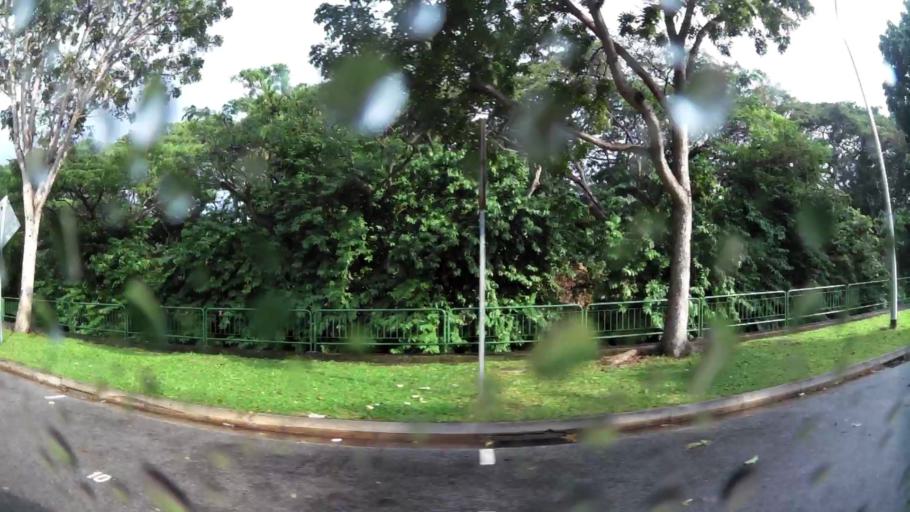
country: SG
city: Singapore
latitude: 1.3323
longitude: 103.9700
